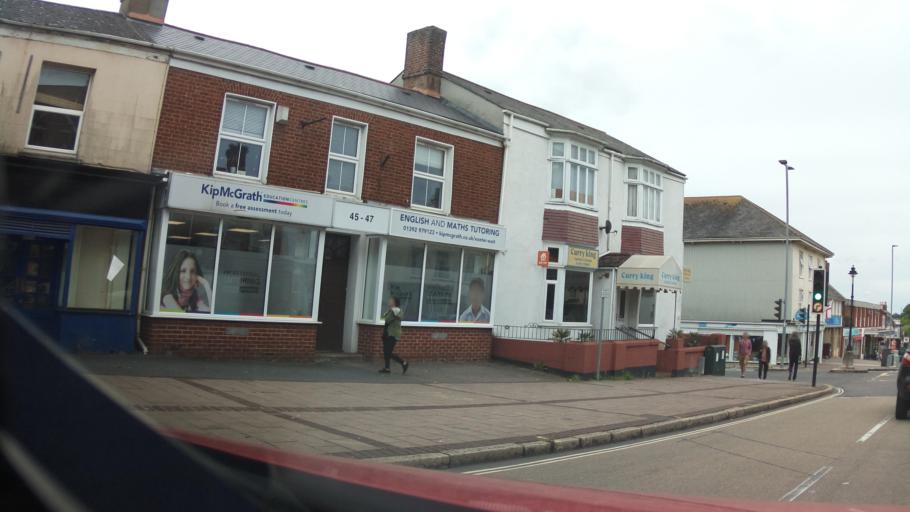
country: GB
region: England
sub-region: Devon
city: Heavitree
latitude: 50.7215
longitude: -3.5061
